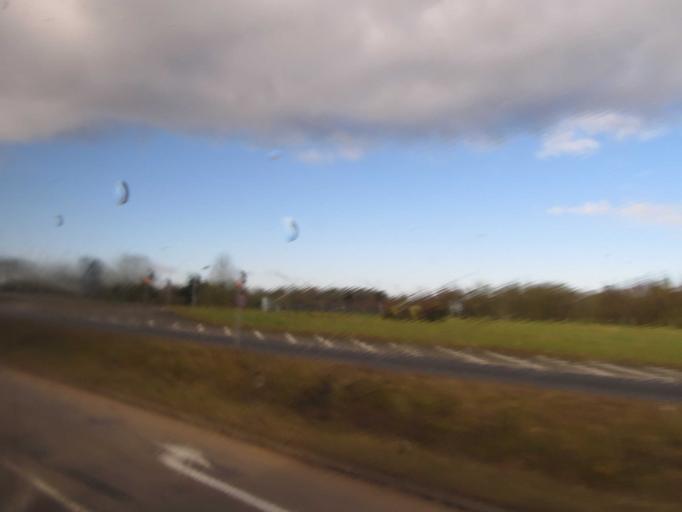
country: GB
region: England
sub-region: Hampshire
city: Basingstoke
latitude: 51.2237
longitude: -1.1570
